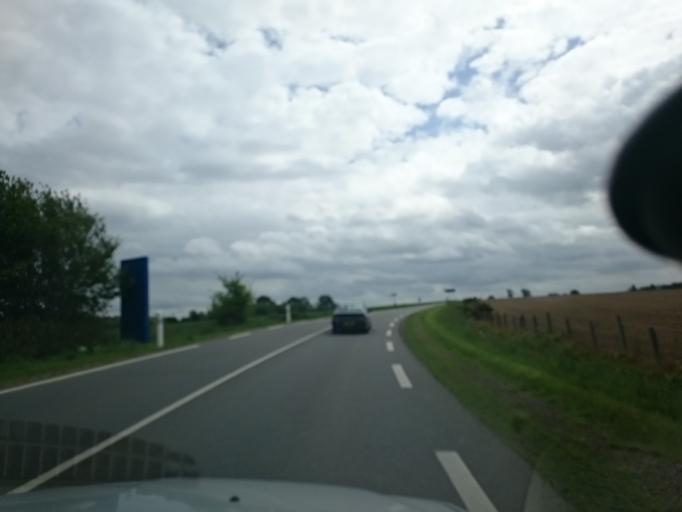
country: FR
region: Brittany
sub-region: Departement d'Ille-et-Vilaine
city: Antrain
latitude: 48.4873
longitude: -1.4669
